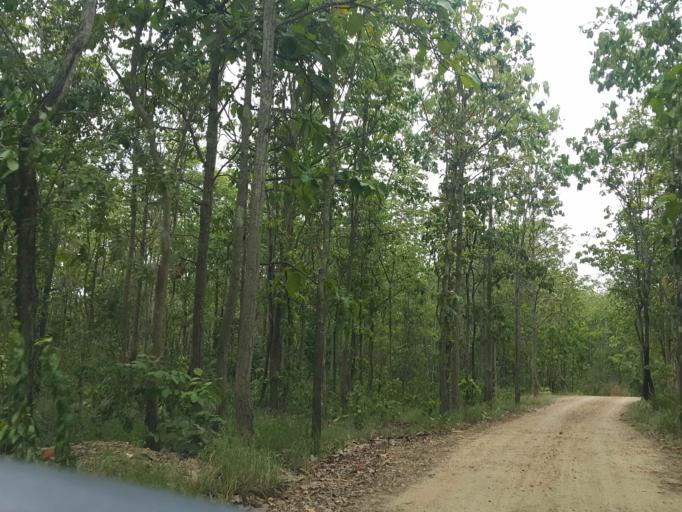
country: TH
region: Chiang Mai
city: Doi Lo
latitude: 18.5003
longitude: 98.7453
